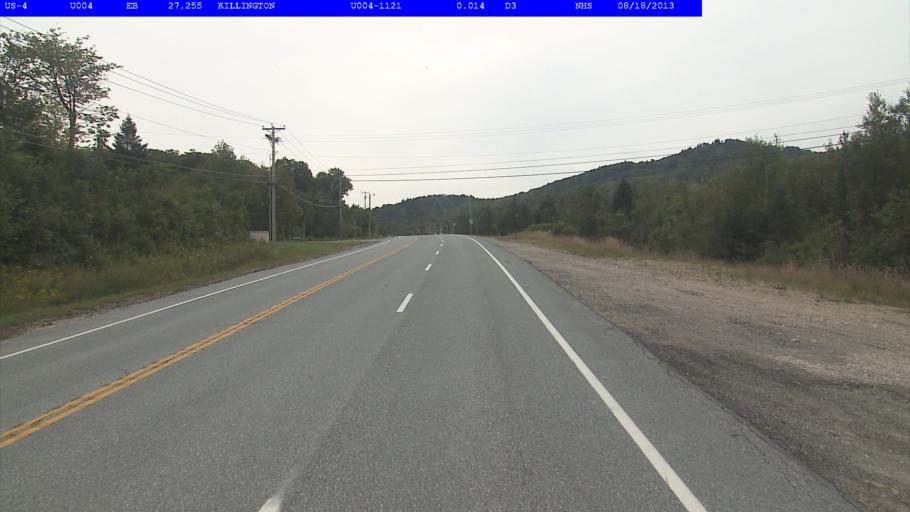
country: US
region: Vermont
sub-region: Rutland County
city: Rutland
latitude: 43.6653
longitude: -72.8462
